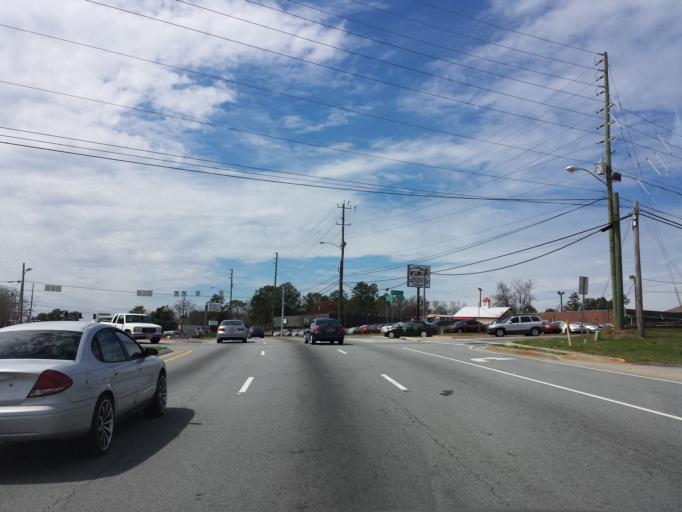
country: US
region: Georgia
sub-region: Cobb County
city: Marietta
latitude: 33.9423
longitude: -84.5169
